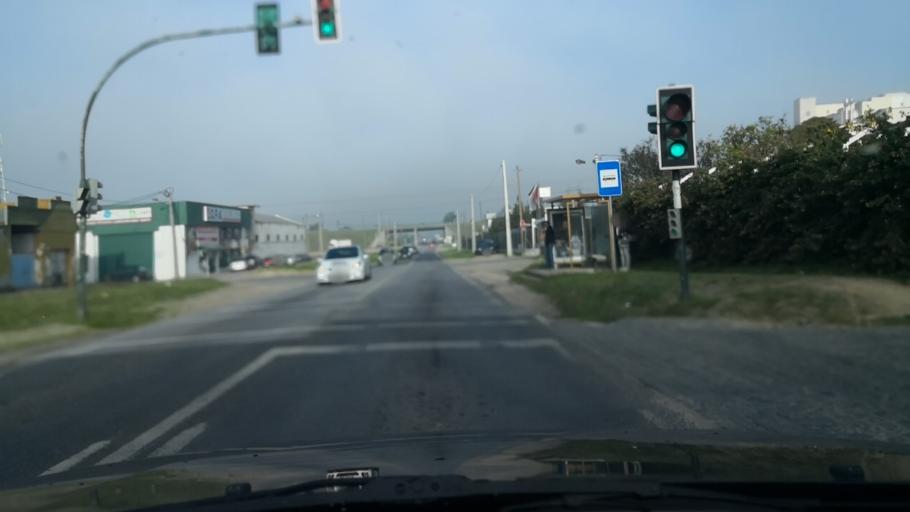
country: PT
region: Setubal
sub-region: Montijo
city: Montijo
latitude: 38.6804
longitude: -8.9391
